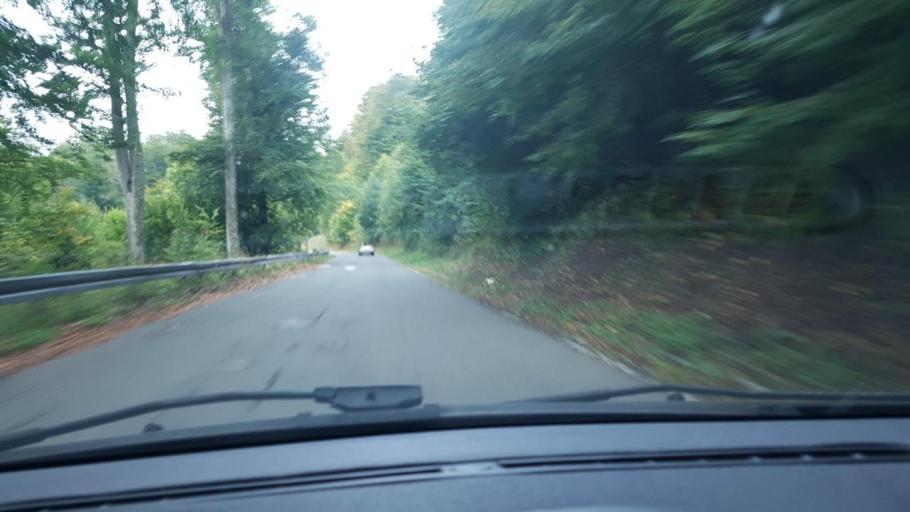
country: HR
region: Grad Zagreb
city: Kasina
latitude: 45.8881
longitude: 15.9350
